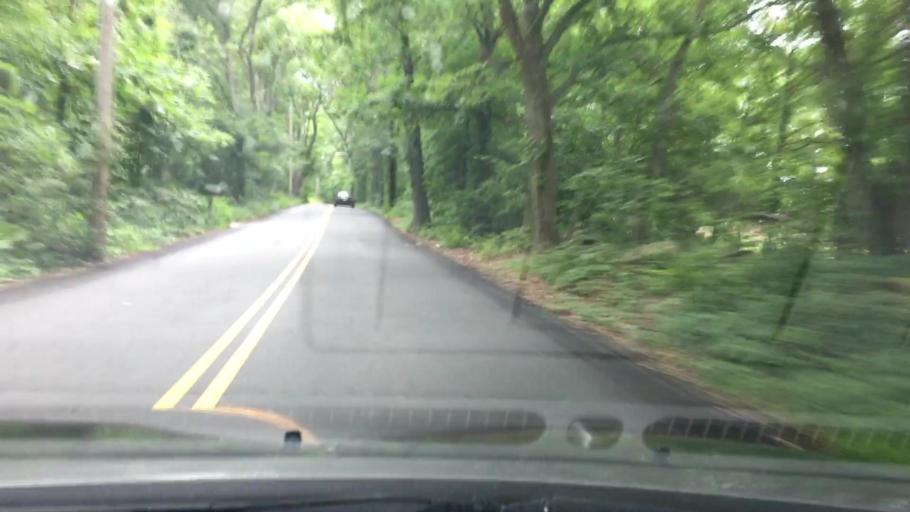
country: US
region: Rhode Island
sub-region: Providence County
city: Cumberland Hill
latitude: 42.0202
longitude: -71.4508
